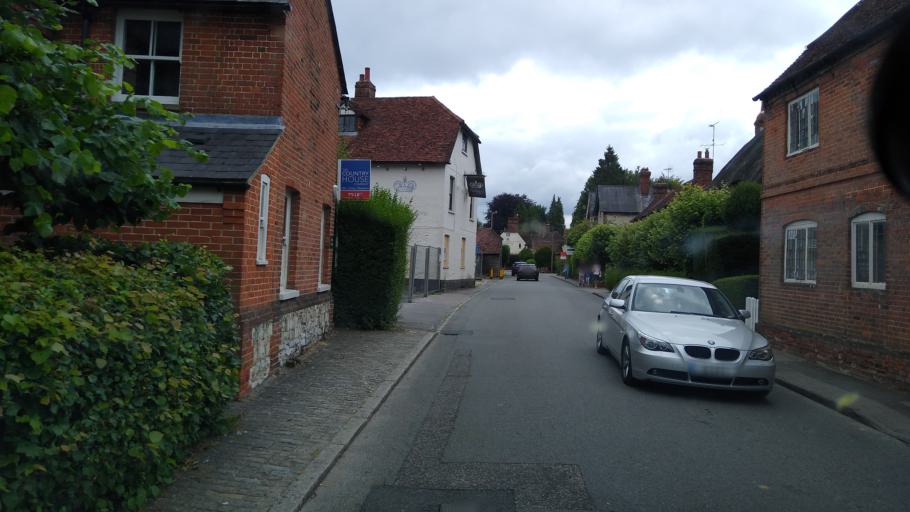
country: GB
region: England
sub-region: Hampshire
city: Alton
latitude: 51.0975
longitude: -0.9430
